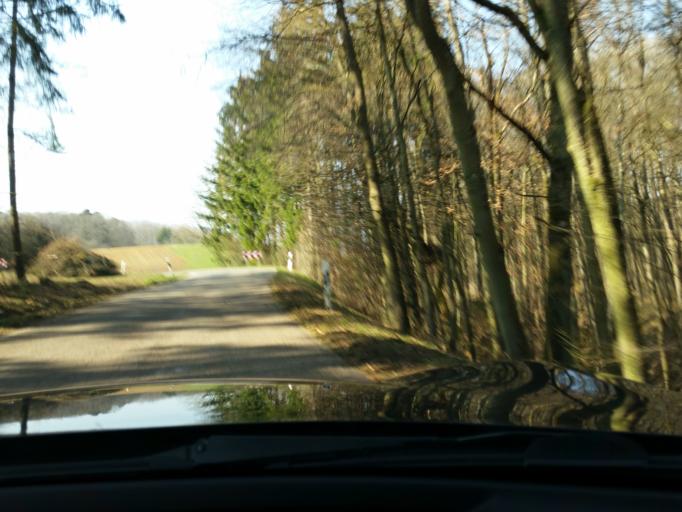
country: DE
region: Baden-Wuerttemberg
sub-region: Regierungsbezirk Stuttgart
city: Jagsthausen
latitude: 49.3614
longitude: 9.4653
